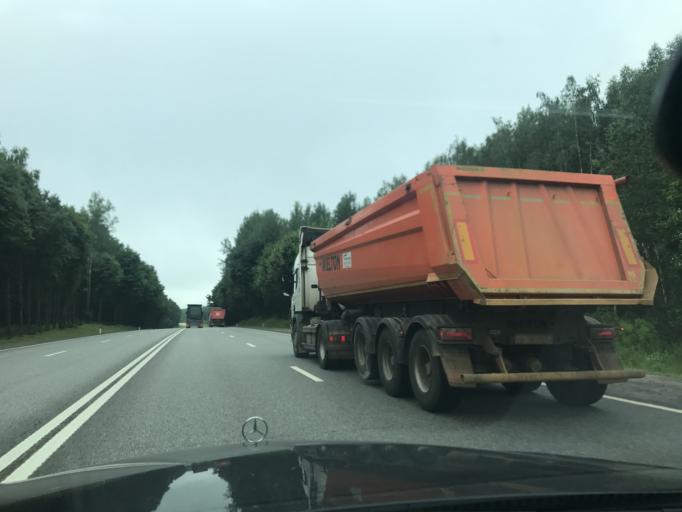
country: RU
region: Smolensk
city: Vyaz'ma
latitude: 55.3190
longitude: 34.5436
